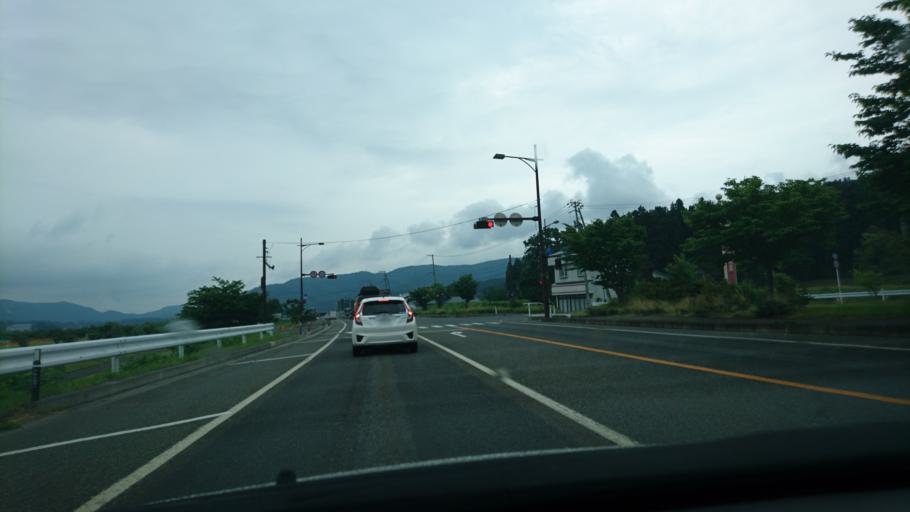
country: JP
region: Miyagi
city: Furukawa
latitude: 38.7386
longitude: 140.7425
